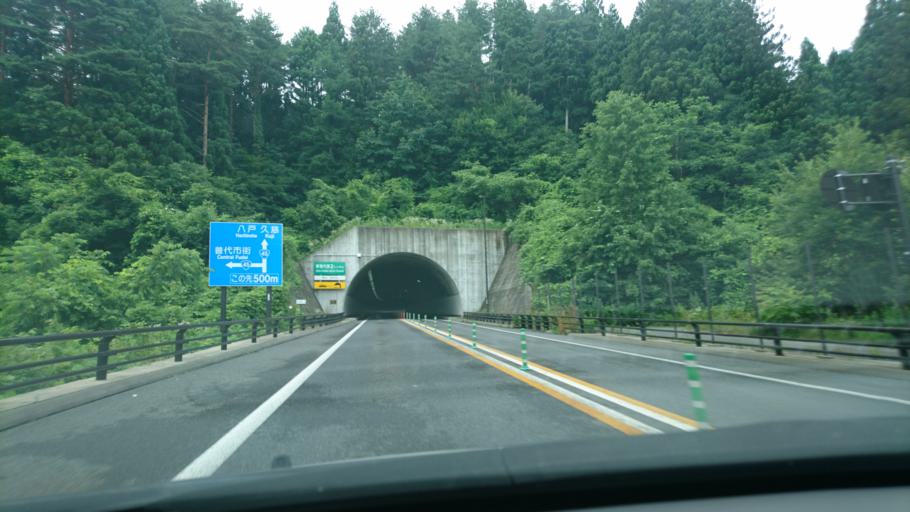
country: JP
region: Iwate
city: Miyako
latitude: 40.0159
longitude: 141.8848
